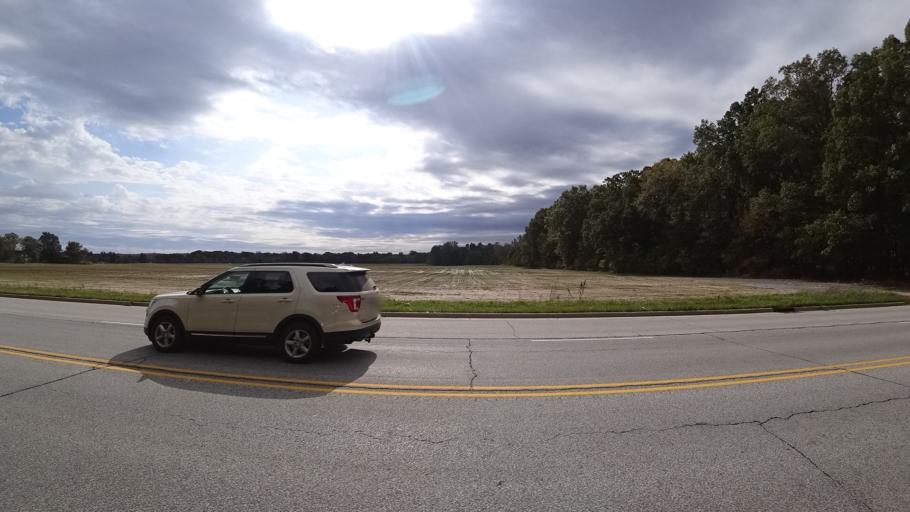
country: US
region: Indiana
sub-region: LaPorte County
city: Trail Creek
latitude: 41.6658
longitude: -86.8788
